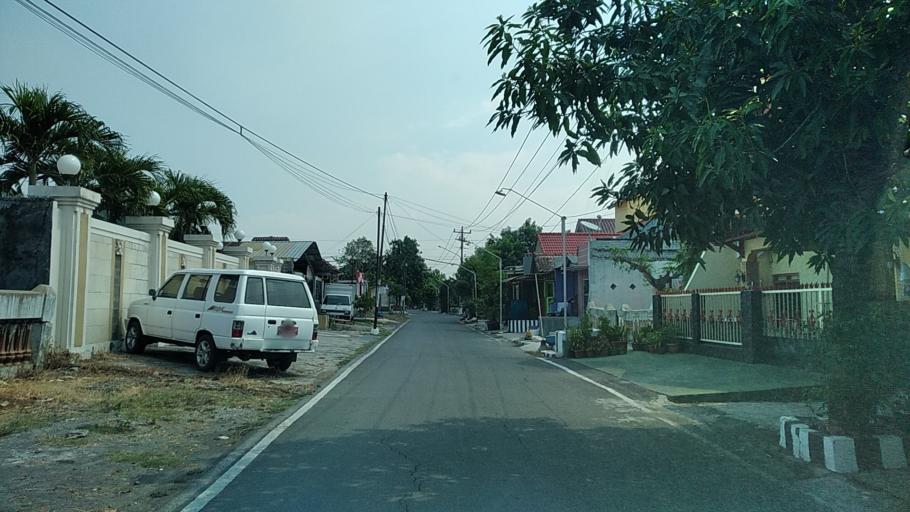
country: ID
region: Central Java
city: Mranggen
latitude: -7.0461
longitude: 110.4812
